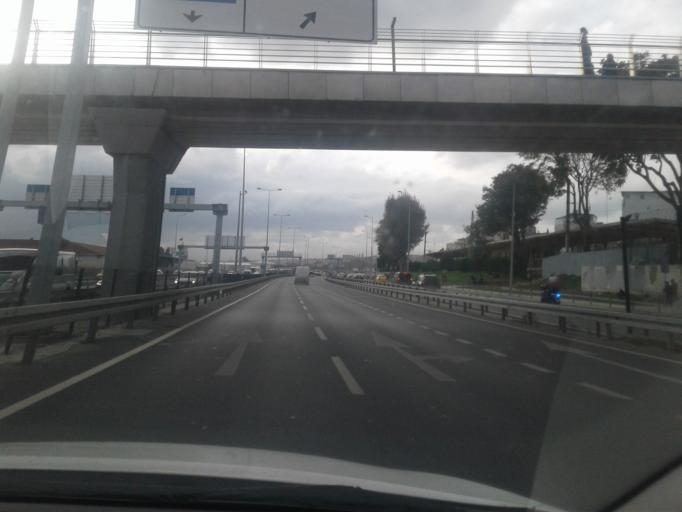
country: TR
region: Istanbul
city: Eminoenue
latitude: 41.0029
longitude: 28.9646
